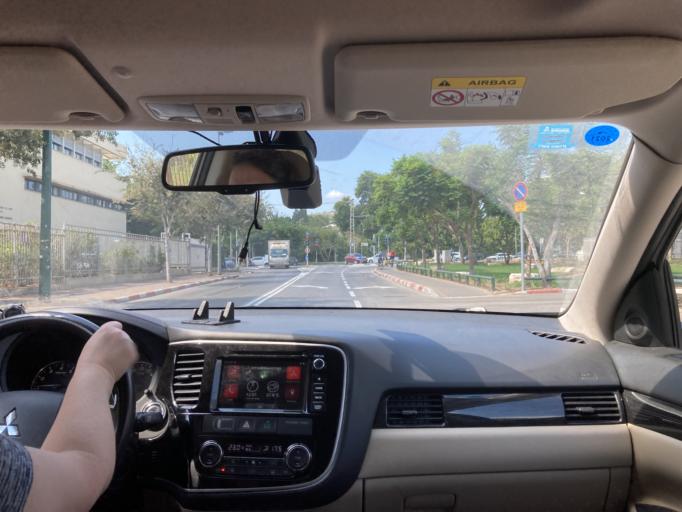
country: IL
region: Tel Aviv
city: Bene Beraq
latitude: 32.1119
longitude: 34.8401
